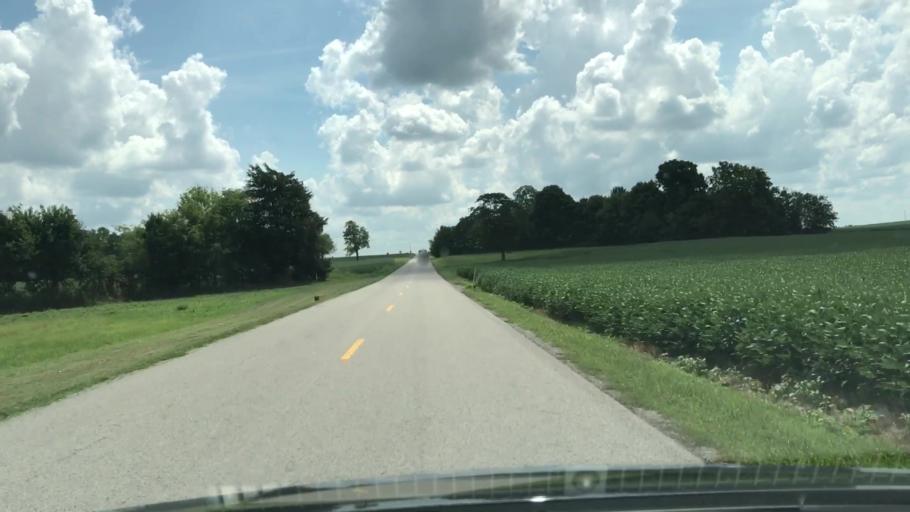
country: US
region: Kentucky
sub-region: Todd County
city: Guthrie
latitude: 36.7022
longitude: -87.0423
